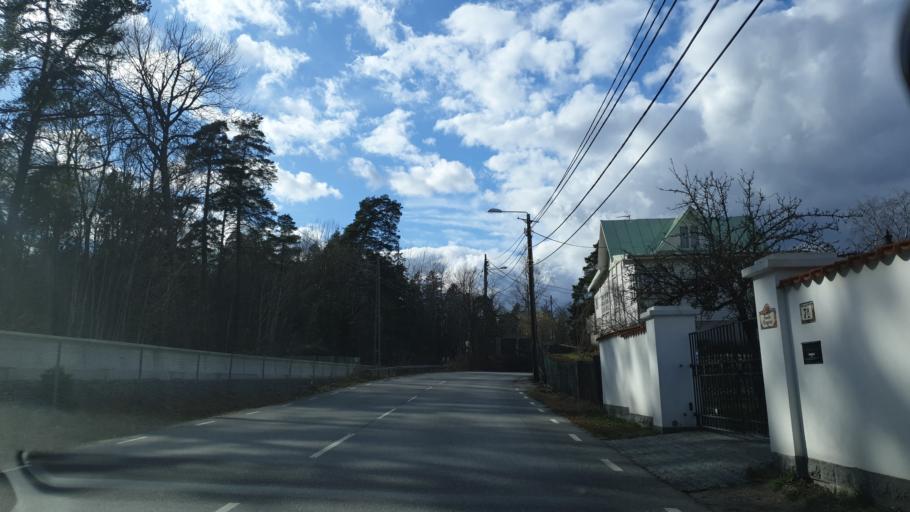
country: SE
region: Stockholm
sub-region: Nacka Kommun
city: Alta
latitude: 59.2989
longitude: 18.2068
